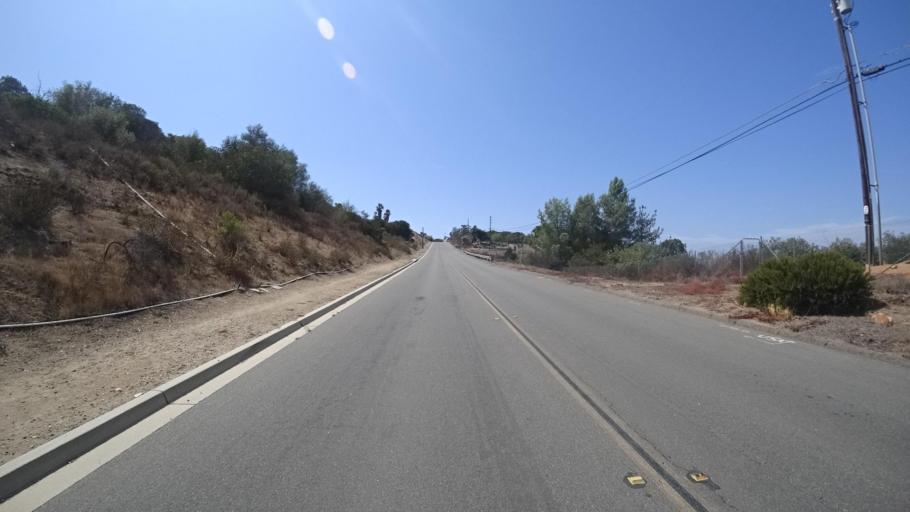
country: US
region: California
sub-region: San Diego County
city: Valley Center
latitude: 33.2112
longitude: -117.0455
